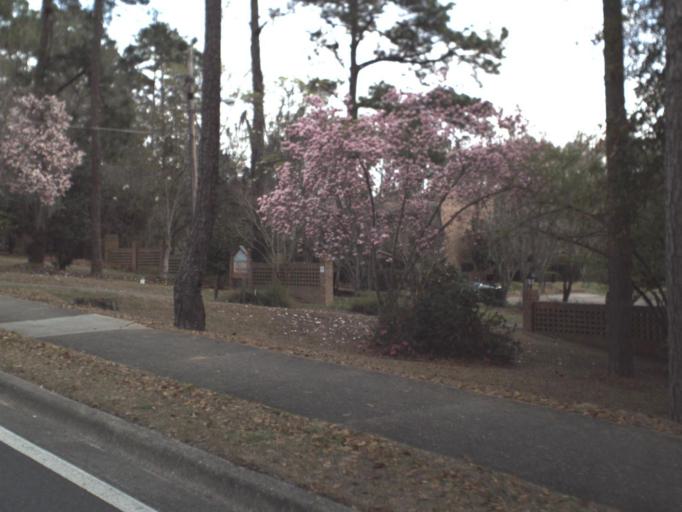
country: US
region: Florida
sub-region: Leon County
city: Tallahassee
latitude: 30.4939
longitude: -84.2545
